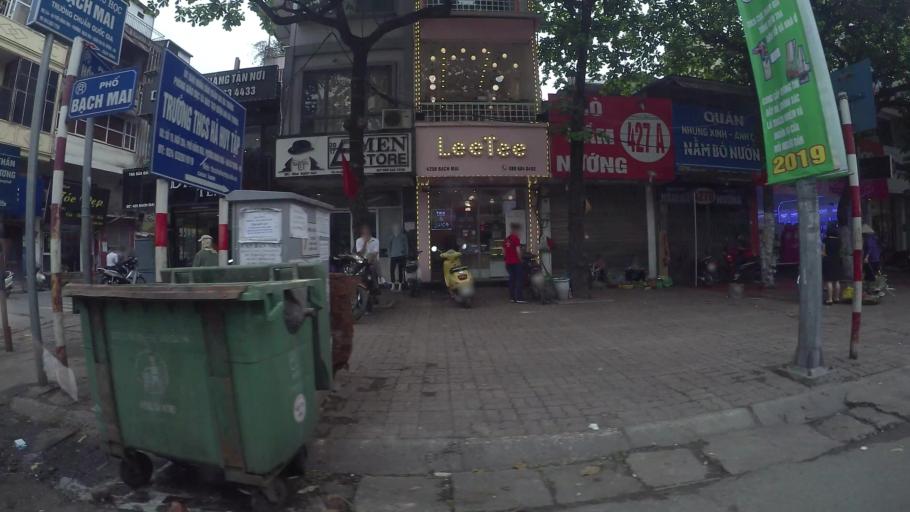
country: VN
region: Ha Noi
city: Hai BaTrung
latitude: 20.9987
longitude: 105.8503
